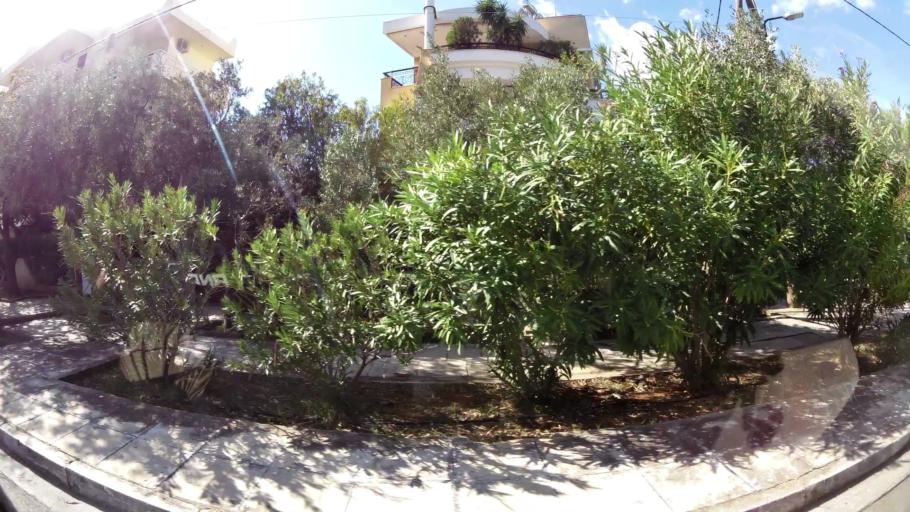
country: GR
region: Attica
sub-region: Nomarchia Anatolikis Attikis
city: Voula
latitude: 37.8536
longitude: 23.7743
